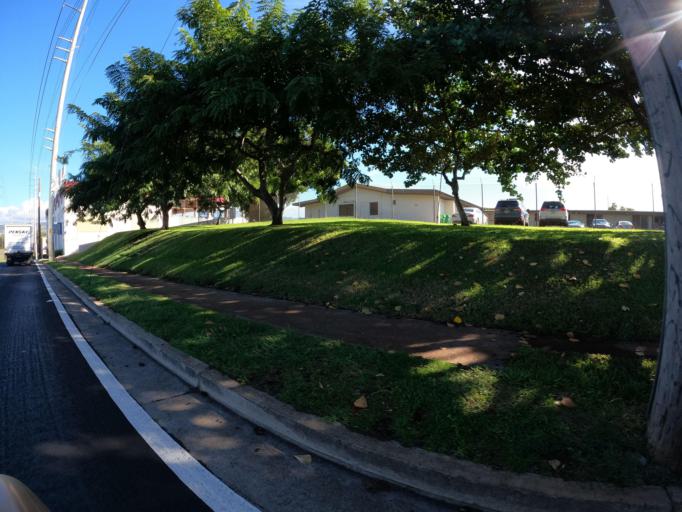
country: US
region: Hawaii
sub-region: Honolulu County
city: Halawa
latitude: 21.3524
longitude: -157.9318
